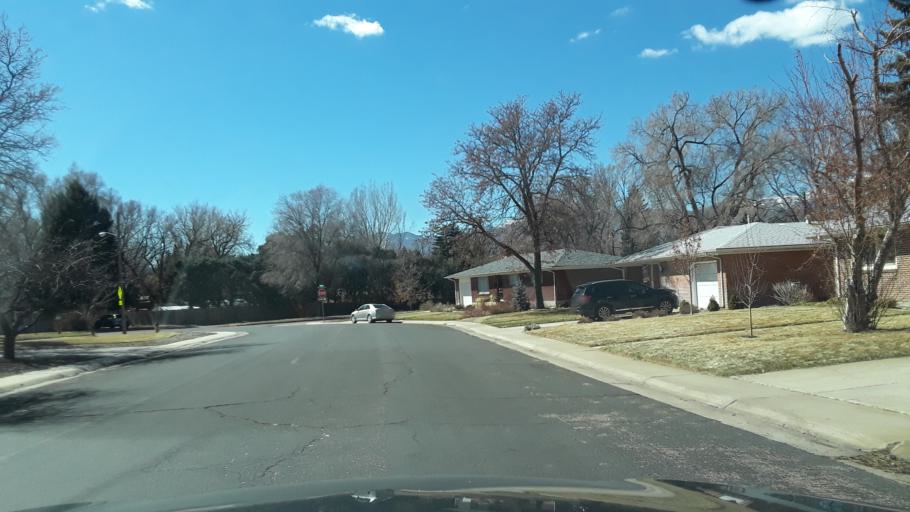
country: US
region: Colorado
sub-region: El Paso County
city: Colorado Springs
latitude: 38.8756
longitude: -104.7987
